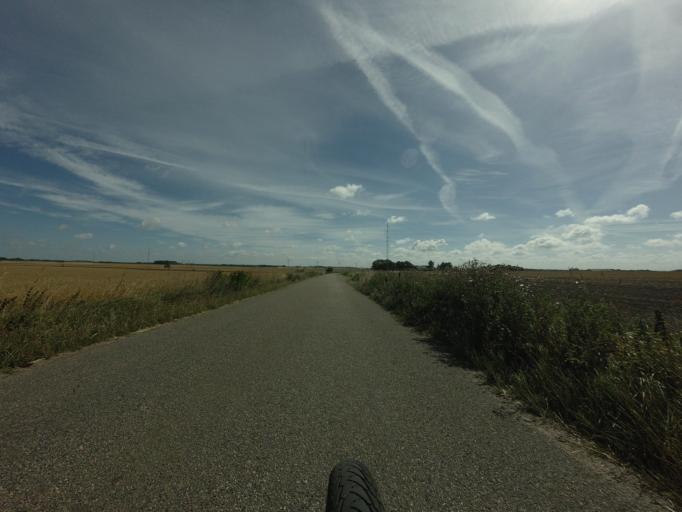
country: DK
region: North Denmark
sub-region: Hjorring Kommune
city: Vra
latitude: 57.3426
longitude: 9.7921
